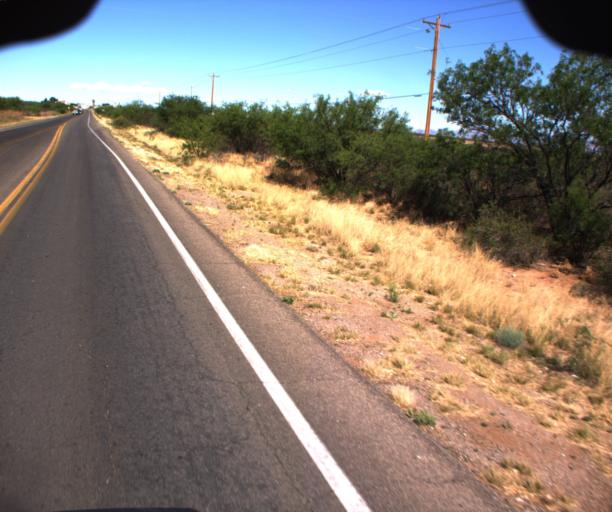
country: US
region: Arizona
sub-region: Cochise County
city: Sierra Vista Southeast
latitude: 31.5534
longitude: -110.1994
